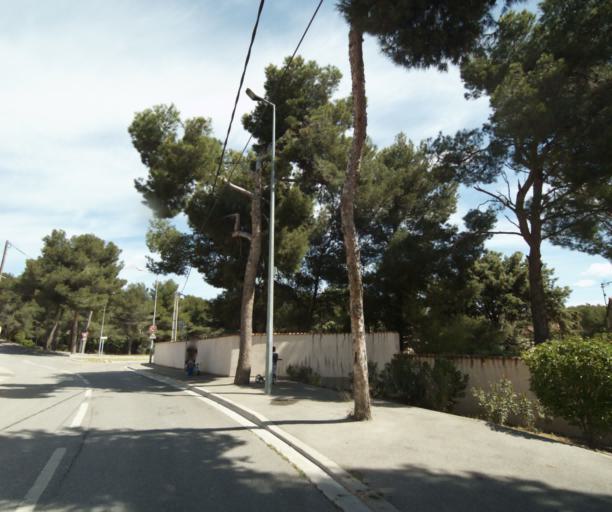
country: FR
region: Provence-Alpes-Cote d'Azur
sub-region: Departement des Bouches-du-Rhone
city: Rognac
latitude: 43.5094
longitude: 5.2187
